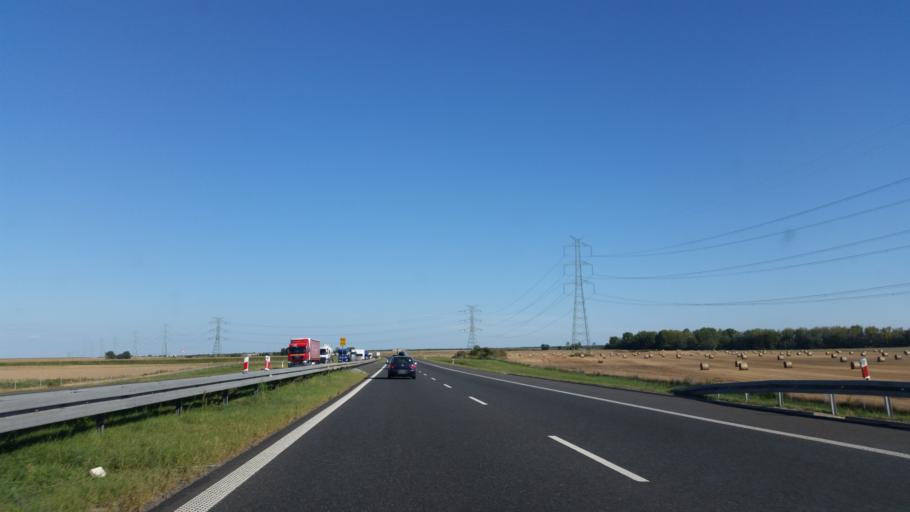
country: PL
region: Opole Voivodeship
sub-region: Powiat brzeski
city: Olszanka
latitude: 50.7463
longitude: 17.4498
